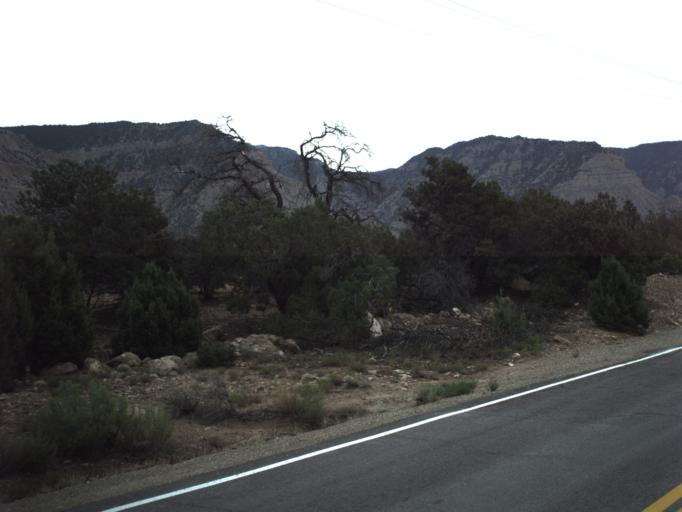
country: US
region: Utah
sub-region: Carbon County
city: East Carbon City
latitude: 39.5285
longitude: -110.4001
